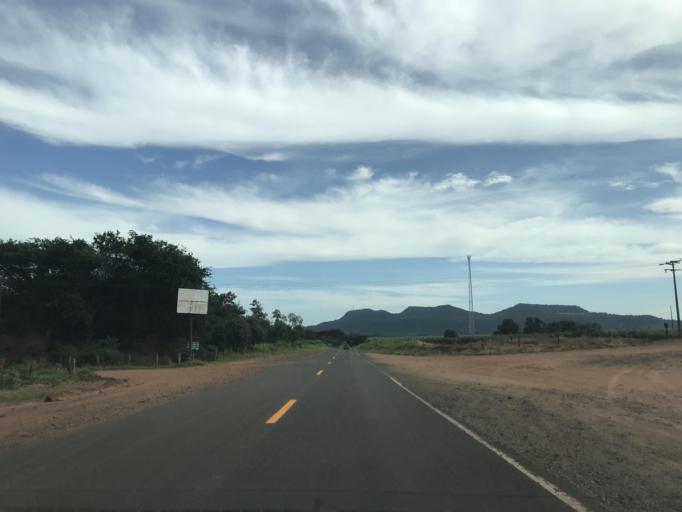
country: BR
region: Parana
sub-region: Paranavai
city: Nova Aurora
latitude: -22.8208
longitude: -52.6550
